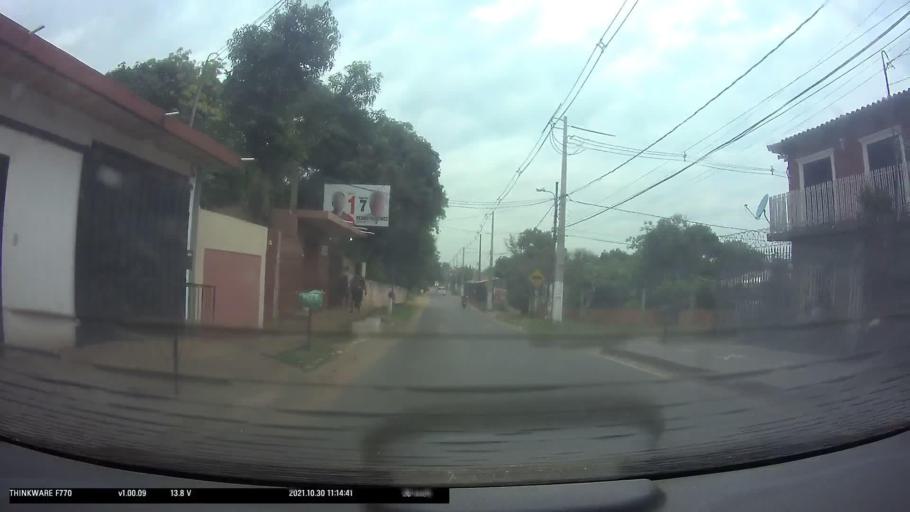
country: PY
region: Central
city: San Lorenzo
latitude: -25.3123
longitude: -57.5122
